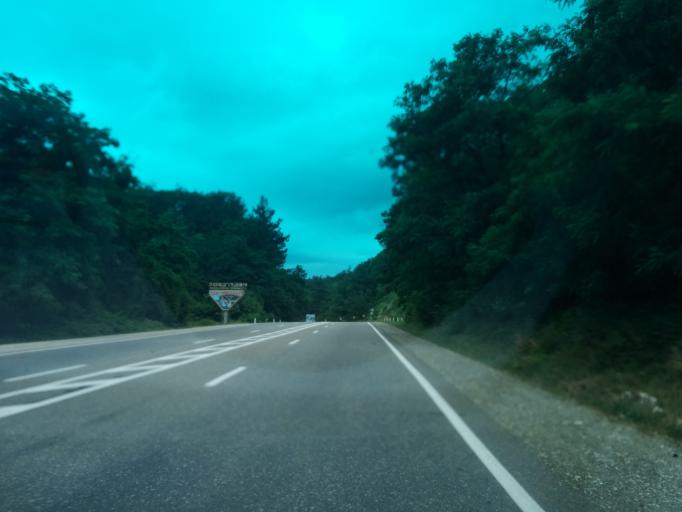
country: RU
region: Krasnodarskiy
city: Ol'ginka
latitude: 44.1812
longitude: 38.9354
